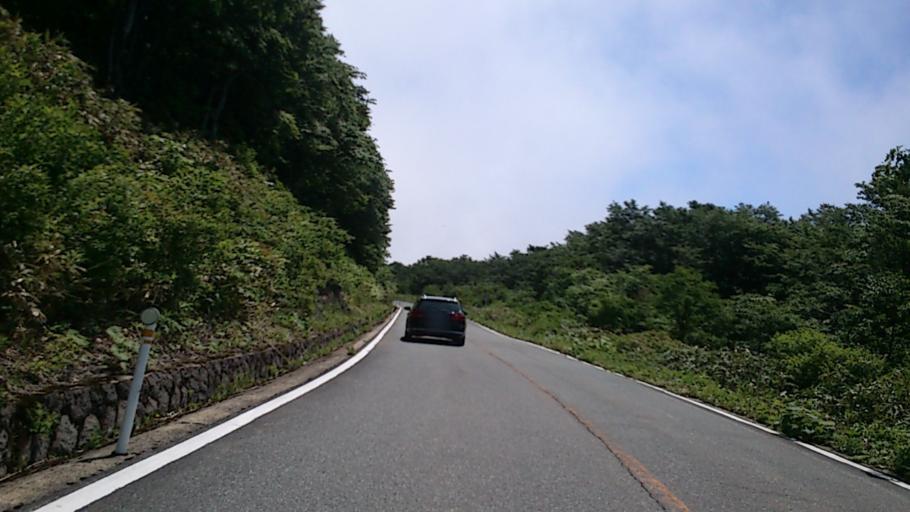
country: JP
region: Yamagata
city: Yamagata-shi
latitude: 38.1204
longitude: 140.4173
